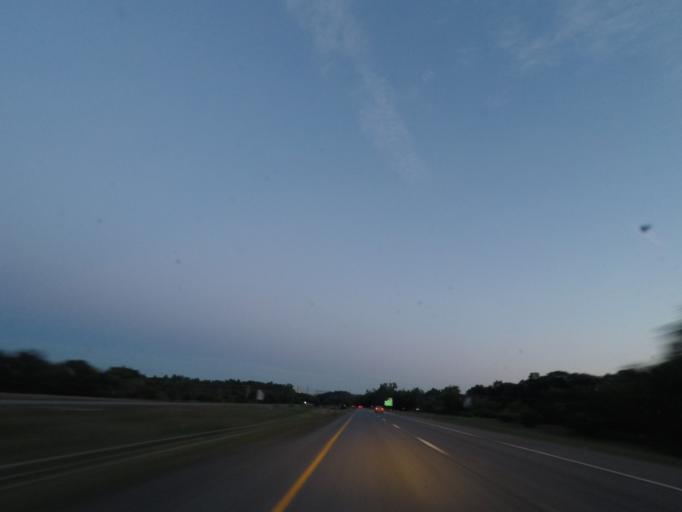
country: US
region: Connecticut
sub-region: Windham County
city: Putnam
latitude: 41.8869
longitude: -71.8965
